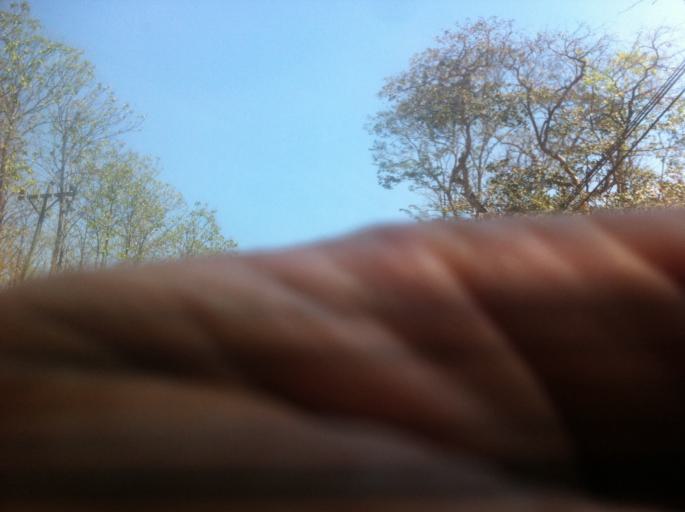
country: CR
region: Guanacaste
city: Hojancha
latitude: 10.0725
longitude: -85.4708
